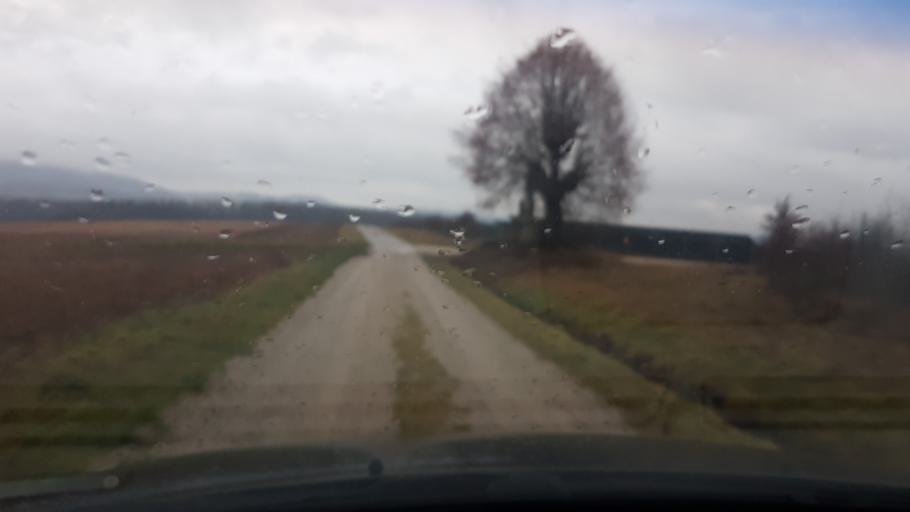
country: DE
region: Bavaria
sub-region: Upper Franconia
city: Zapfendorf
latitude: 50.0278
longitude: 10.9632
